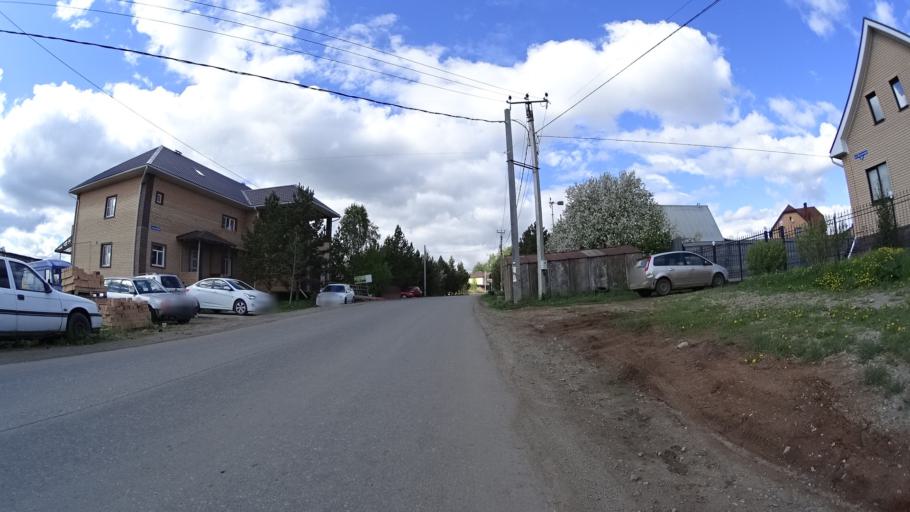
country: RU
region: Chelyabinsk
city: Sargazy
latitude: 55.1561
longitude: 61.2414
